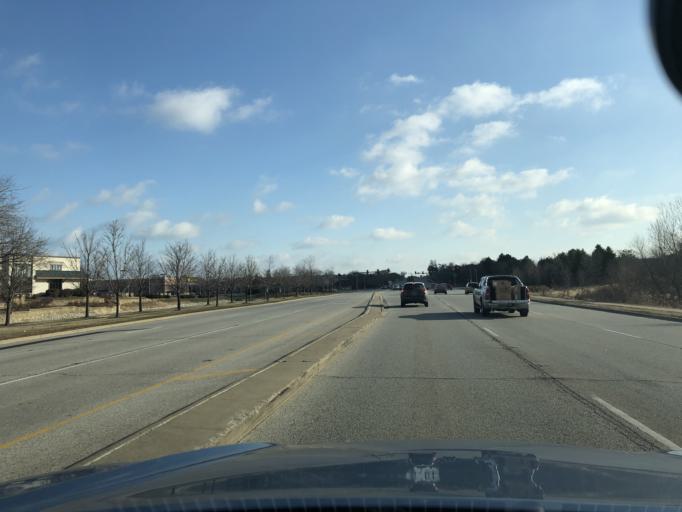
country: US
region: Illinois
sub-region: Cook County
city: Northfield
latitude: 42.1055
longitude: -87.8091
